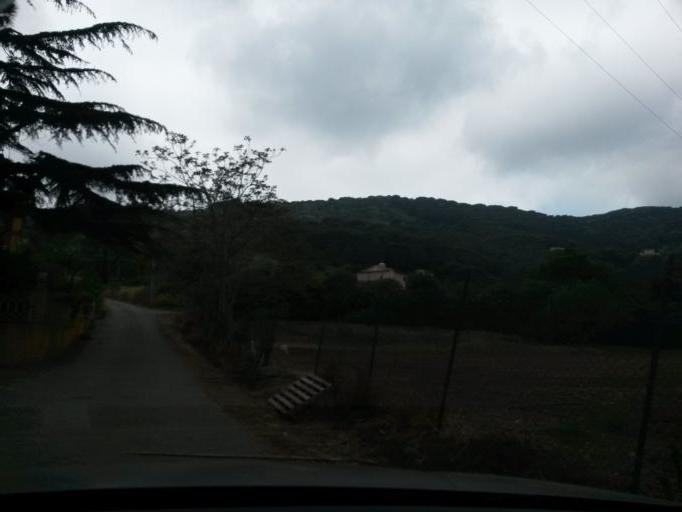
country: IT
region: Tuscany
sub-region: Provincia di Livorno
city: Porto Azzurro
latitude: 42.7735
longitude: 10.3870
